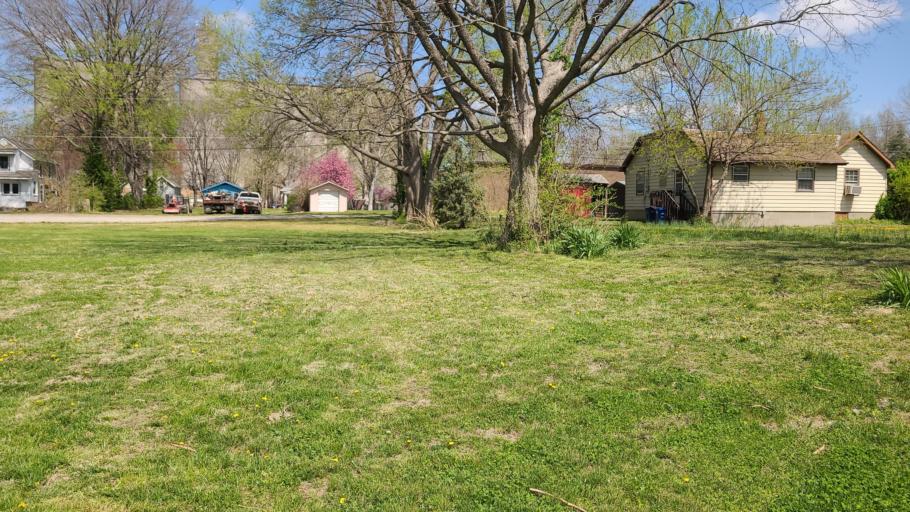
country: US
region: Kansas
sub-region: Douglas County
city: Lawrence
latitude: 38.9760
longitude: -95.2317
